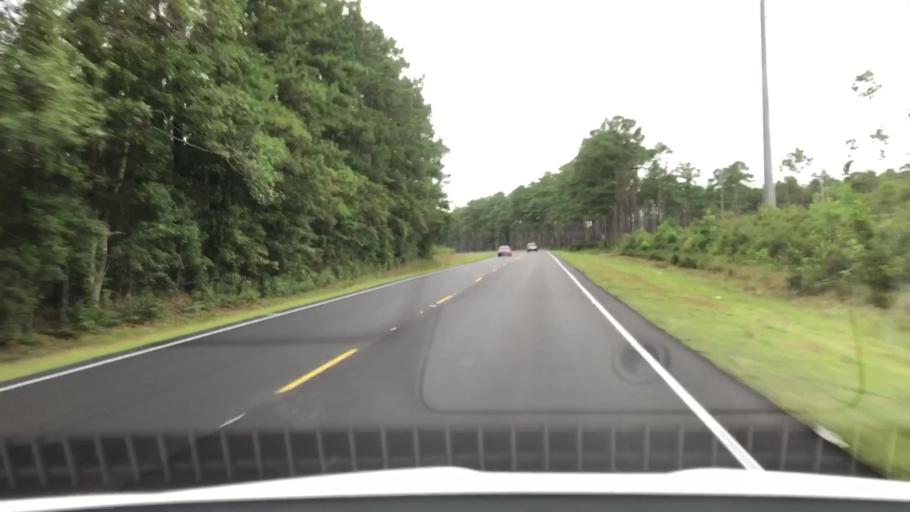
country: US
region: North Carolina
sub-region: Onslow County
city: Swansboro
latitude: 34.7703
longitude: -77.0972
